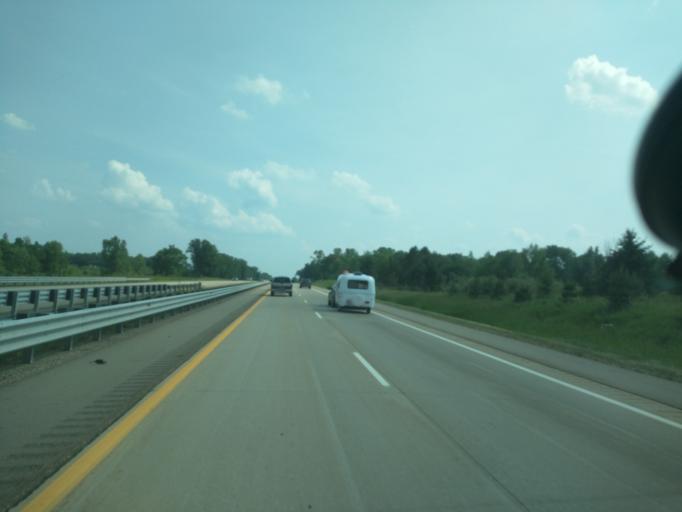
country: US
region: Michigan
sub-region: Ingham County
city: Leslie
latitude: 42.3493
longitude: -84.4290
